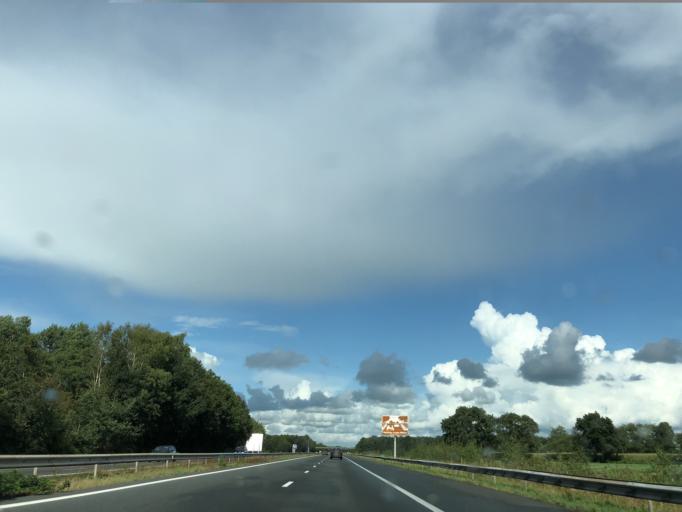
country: NL
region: Friesland
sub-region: Gemeente Smallingerland
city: Drachtstercompagnie
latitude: 53.1117
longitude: 6.1503
